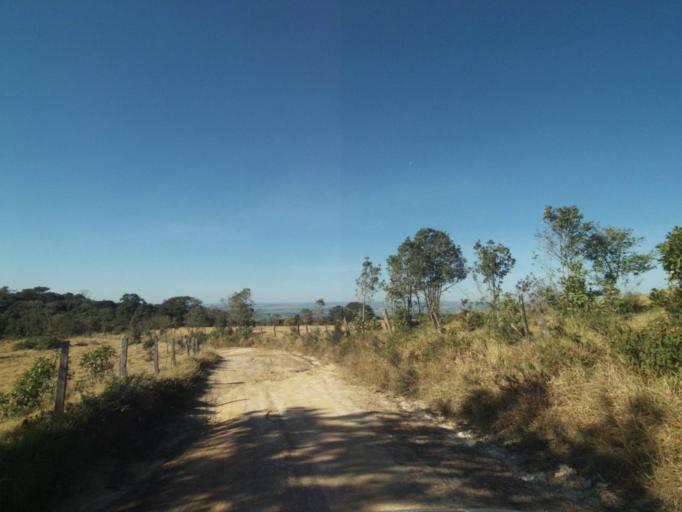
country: BR
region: Parana
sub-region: Tibagi
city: Tibagi
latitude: -24.5500
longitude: -50.4704
